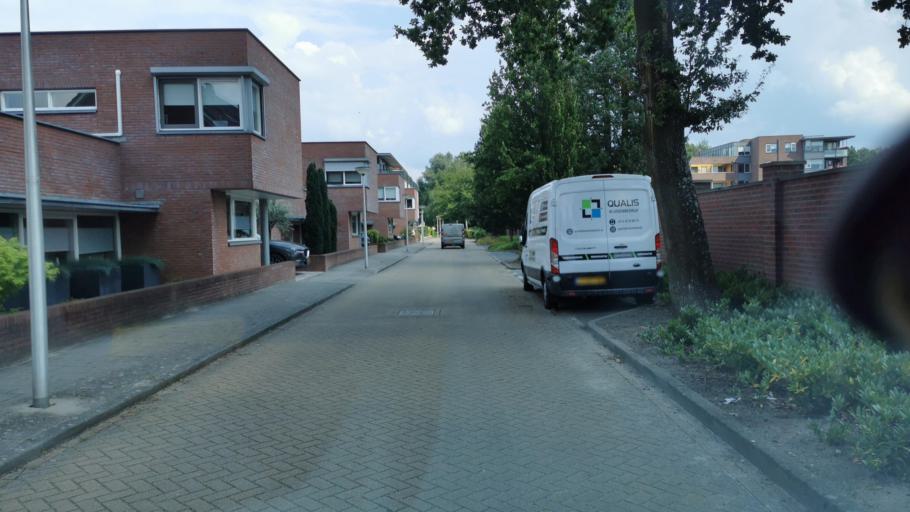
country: DE
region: North Rhine-Westphalia
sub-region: Regierungsbezirk Munster
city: Gronau
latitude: 52.2197
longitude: 6.9713
